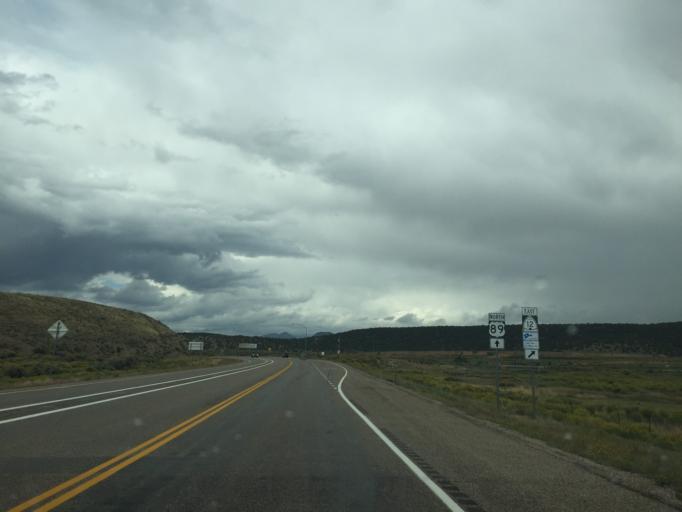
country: US
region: Utah
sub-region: Garfield County
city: Panguitch
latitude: 37.7471
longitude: -112.3781
